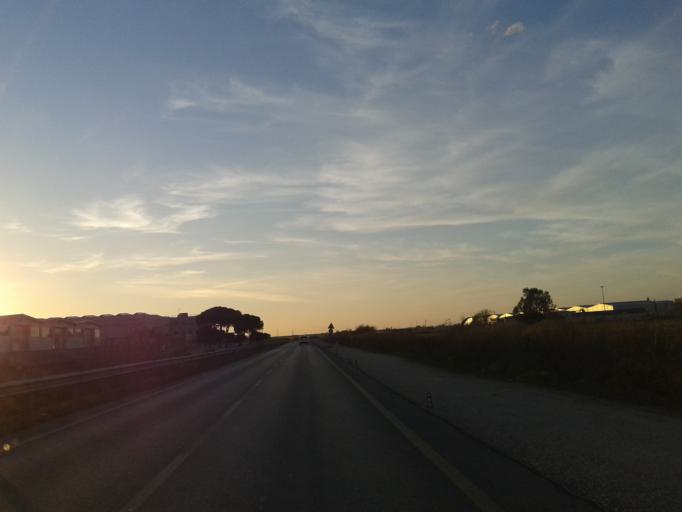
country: IT
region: Tuscany
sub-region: Provincia di Livorno
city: Guasticce
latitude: 43.5968
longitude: 10.3845
